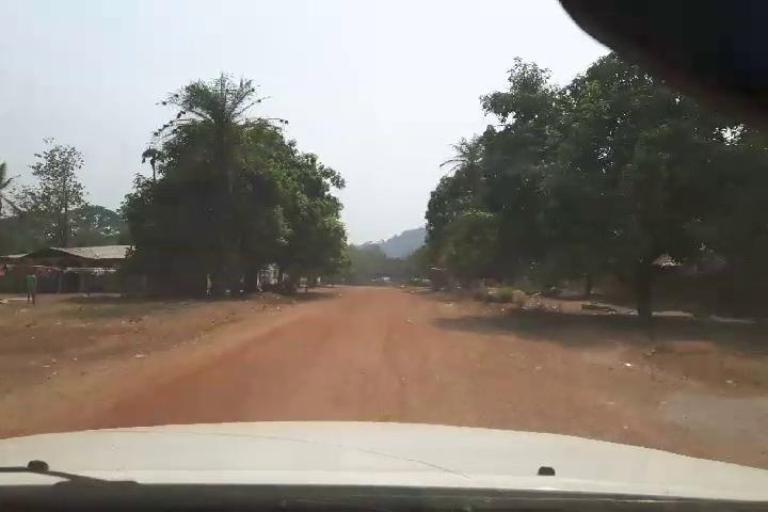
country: SL
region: Northern Province
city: Bumbuna
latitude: 8.9483
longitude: -11.8105
